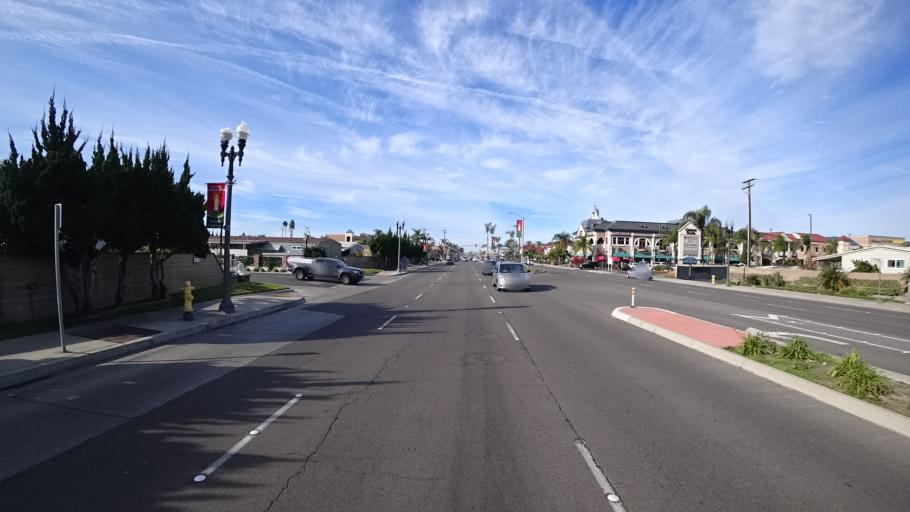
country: US
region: California
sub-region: Orange County
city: Midway City
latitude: 33.7448
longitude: -117.9586
